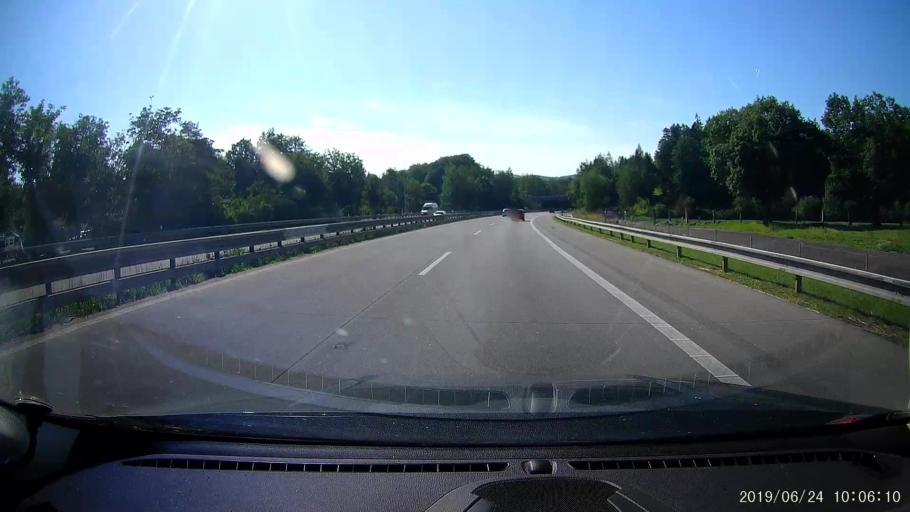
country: CZ
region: Central Bohemia
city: Divisov
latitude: 49.7960
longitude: 14.9208
